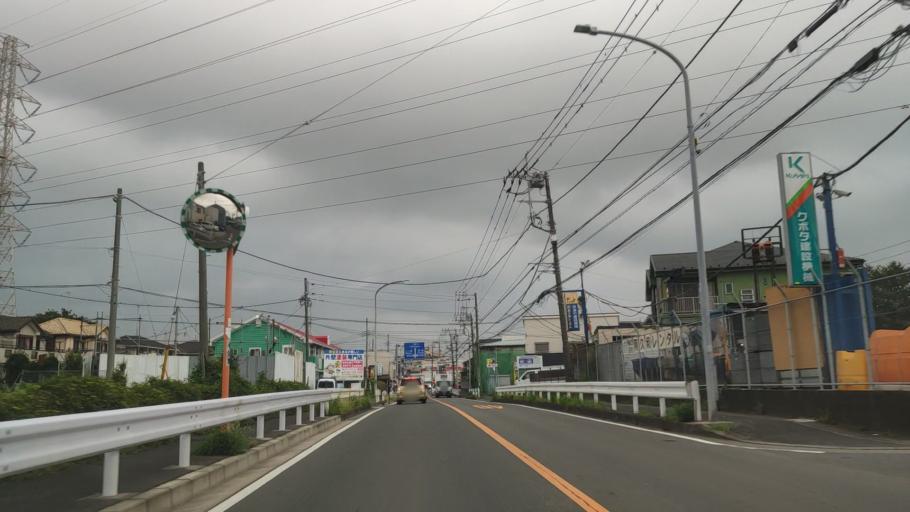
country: JP
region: Kanagawa
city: Minami-rinkan
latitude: 35.4453
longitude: 139.4981
